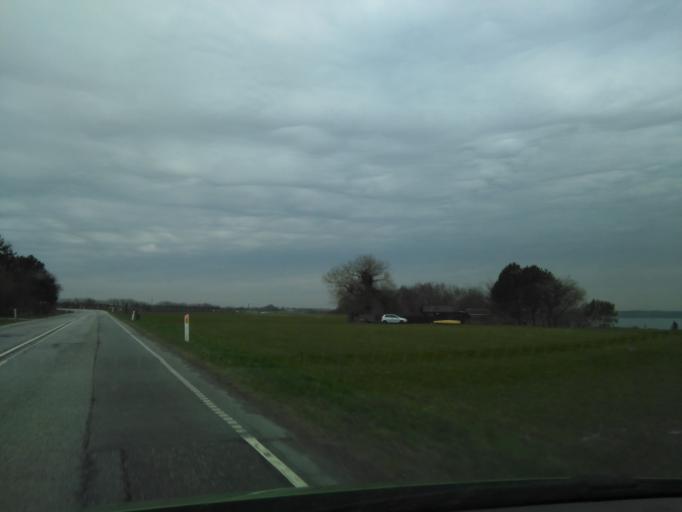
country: DK
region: North Denmark
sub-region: Mariagerfjord Kommune
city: Hadsund
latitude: 56.6862
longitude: 10.0974
